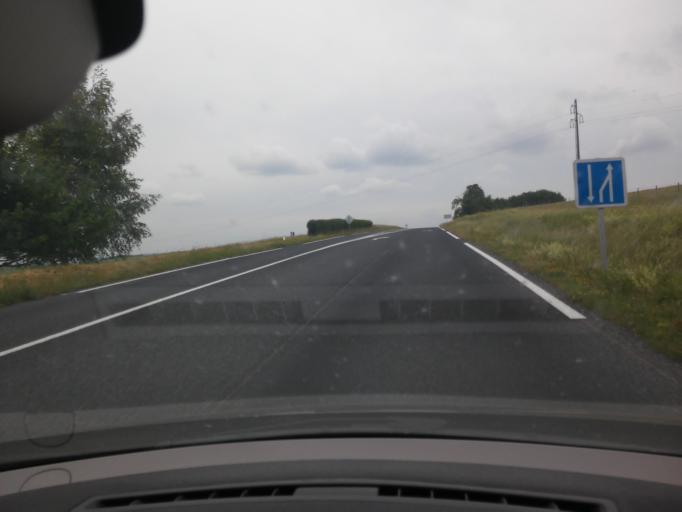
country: FR
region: Lorraine
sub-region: Departement de la Meuse
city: Saint-Mihiel
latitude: 48.8748
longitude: 5.5231
